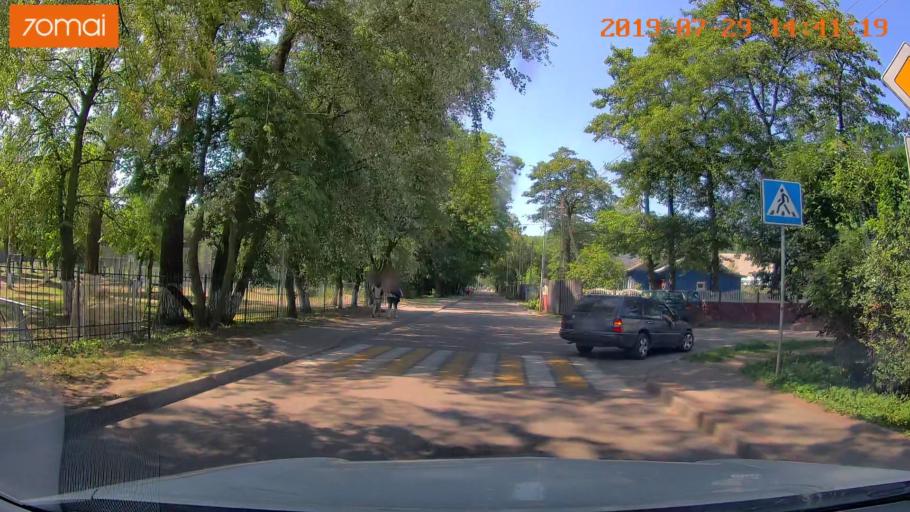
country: RU
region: Kaliningrad
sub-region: Gorod Kaliningrad
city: Baltiysk
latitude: 54.6572
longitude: 19.8995
